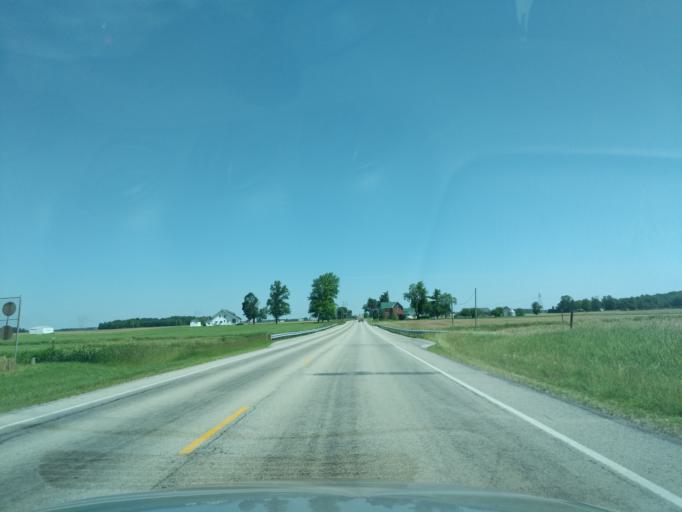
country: US
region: Indiana
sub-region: Huntington County
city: Huntington
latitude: 40.9245
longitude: -85.4709
